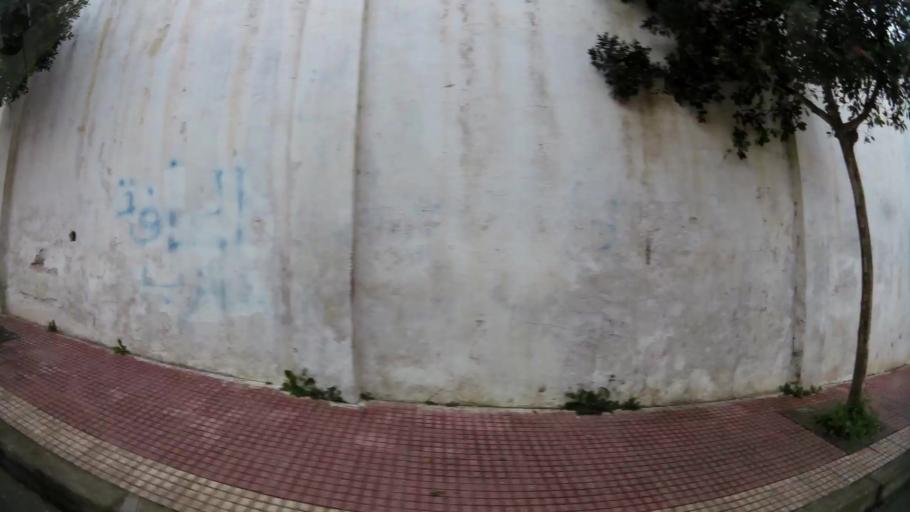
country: MA
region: Tanger-Tetouan
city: Chefchaouene
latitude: 35.1699
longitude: -5.2728
